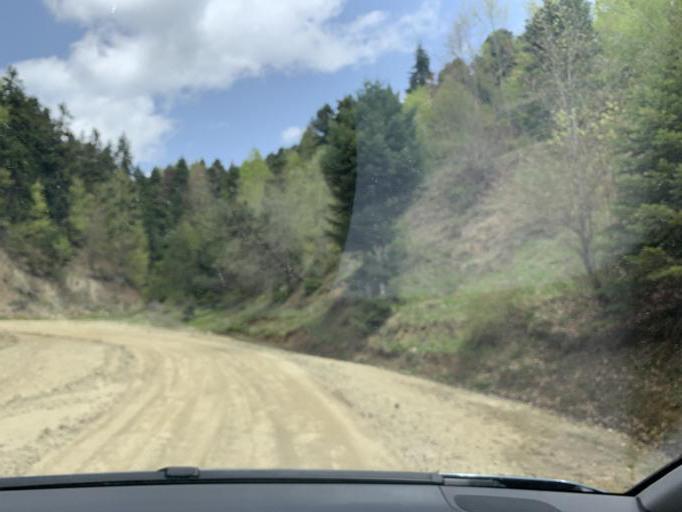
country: TR
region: Bolu
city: Bolu
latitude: 40.8377
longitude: 31.6714
